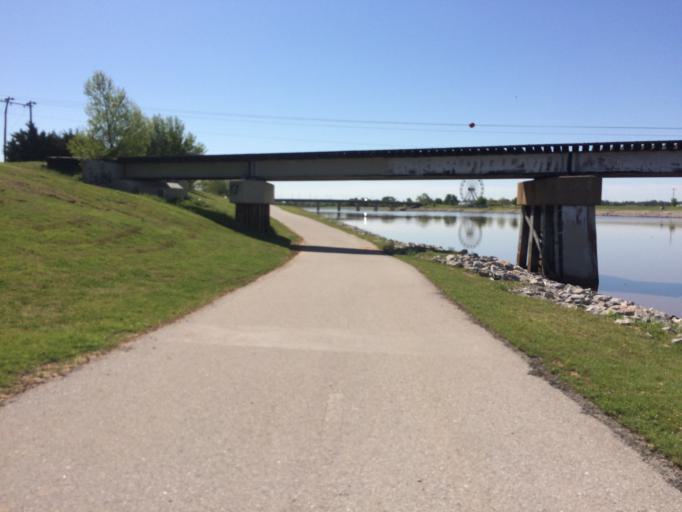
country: US
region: Oklahoma
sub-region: Oklahoma County
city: Oklahoma City
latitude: 35.4567
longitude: -97.5342
